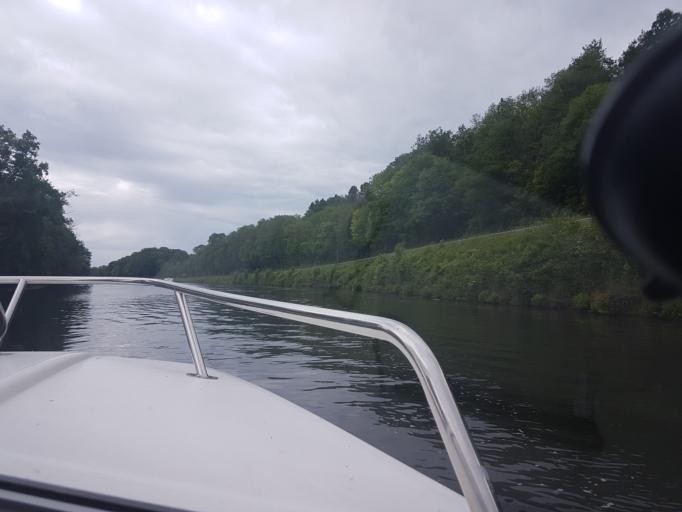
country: FR
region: Bourgogne
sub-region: Departement de l'Yonne
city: Champs-sur-Yonne
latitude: 47.7460
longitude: 3.5866
